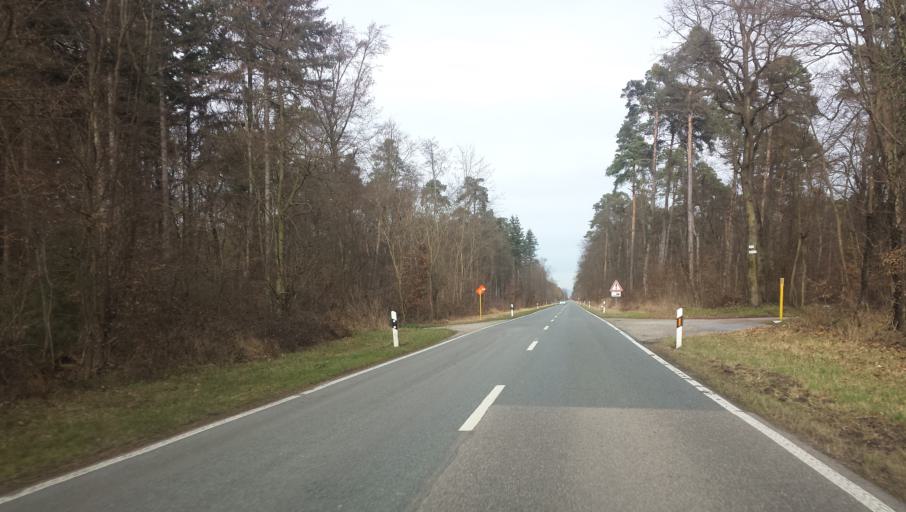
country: DE
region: Baden-Wuerttemberg
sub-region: Karlsruhe Region
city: Waghausel
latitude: 49.2602
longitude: 8.5509
